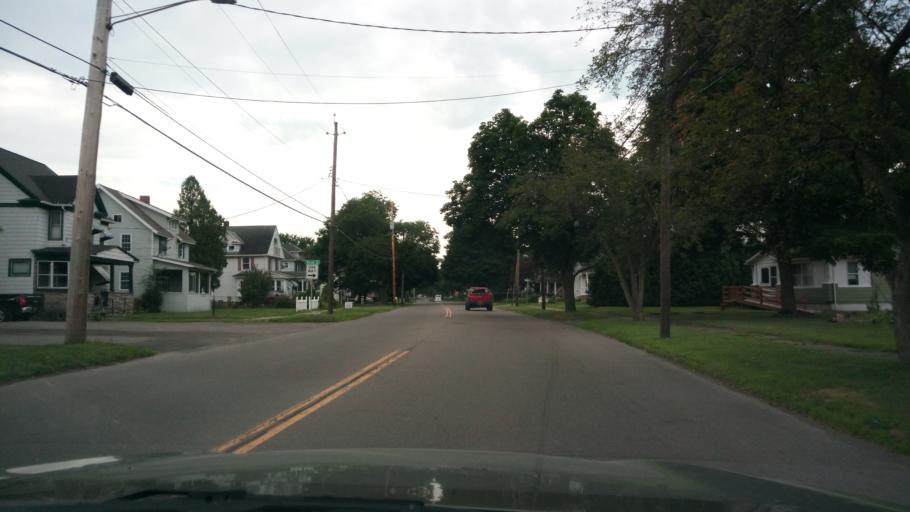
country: US
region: New York
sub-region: Chemung County
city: Elmira Heights
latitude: 42.1148
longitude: -76.8082
